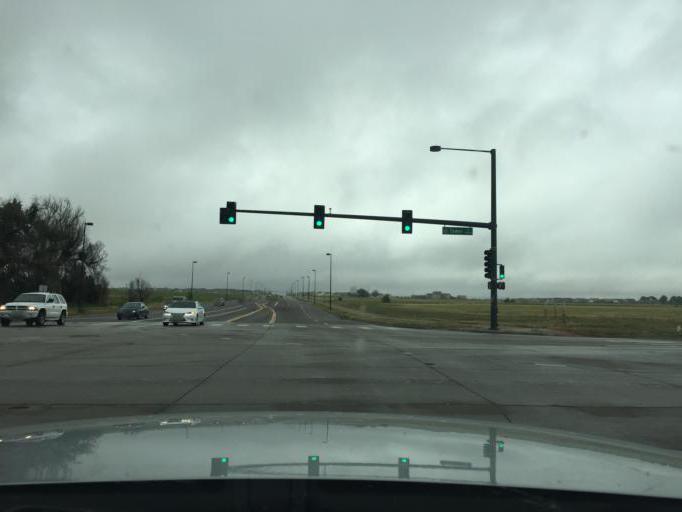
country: US
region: Colorado
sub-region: Adams County
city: Aurora
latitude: 39.7983
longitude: -104.7724
